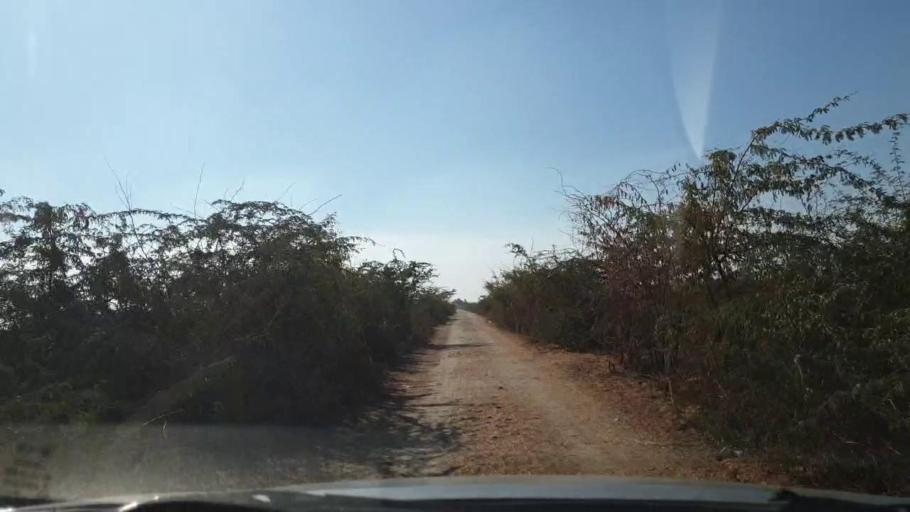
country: PK
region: Sindh
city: Jhol
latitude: 25.8175
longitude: 69.0118
